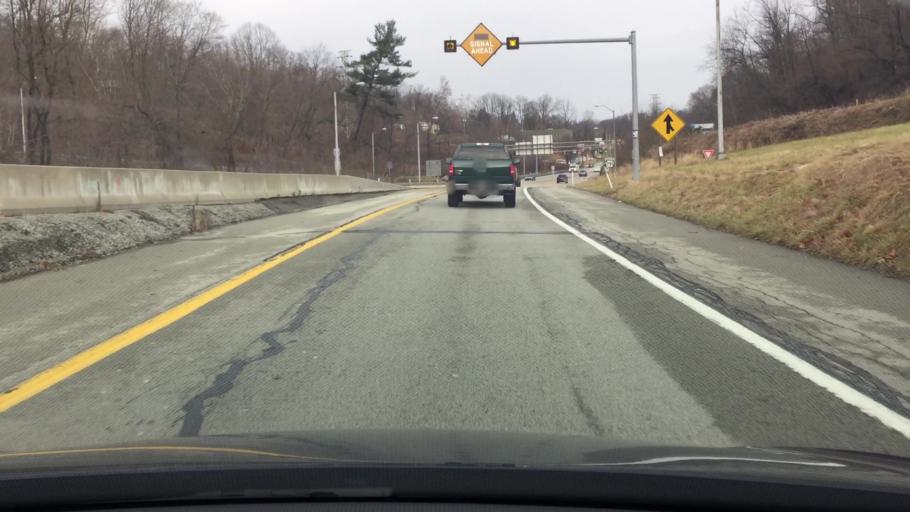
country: US
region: Pennsylvania
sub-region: Allegheny County
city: Churchill
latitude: 40.4425
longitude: -79.8283
